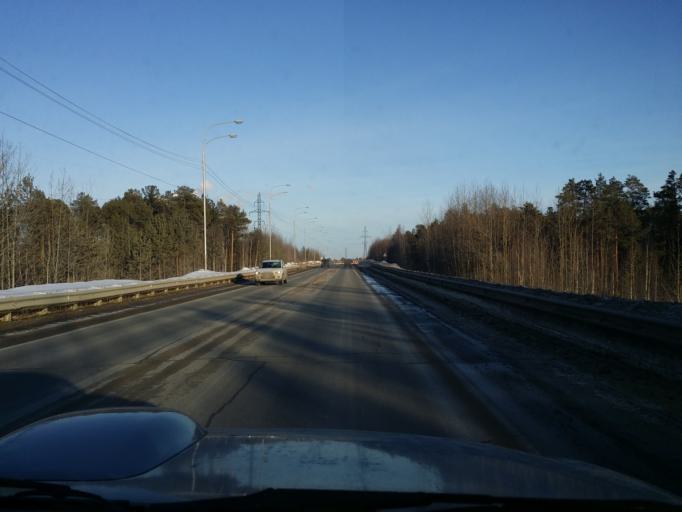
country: RU
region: Khanty-Mansiyskiy Avtonomnyy Okrug
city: Izluchinsk
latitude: 60.9646
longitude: 76.8633
